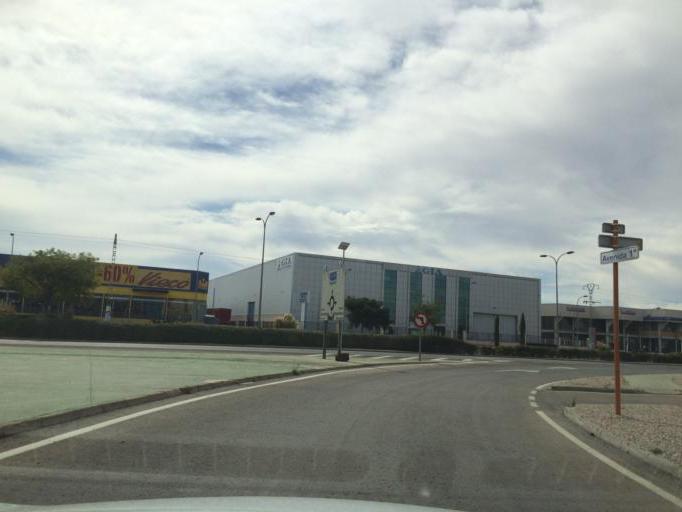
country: ES
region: Castille-La Mancha
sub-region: Provincia de Albacete
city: Albacete
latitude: 39.0204
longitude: -1.8849
